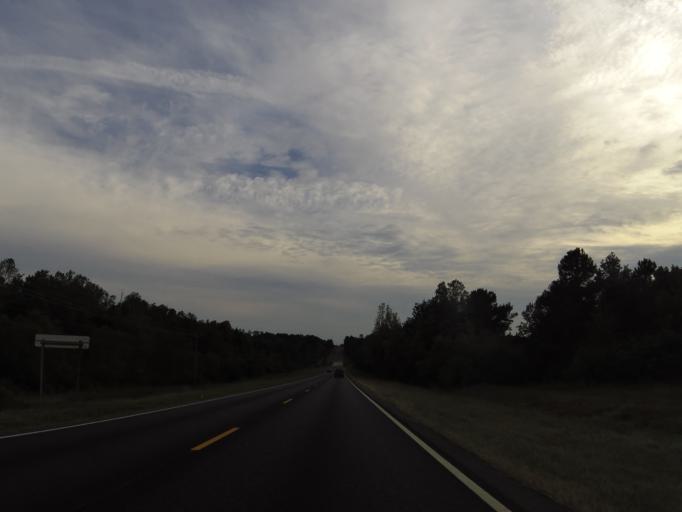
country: US
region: Alabama
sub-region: Escambia County
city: Atmore
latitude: 31.1277
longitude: -87.4653
